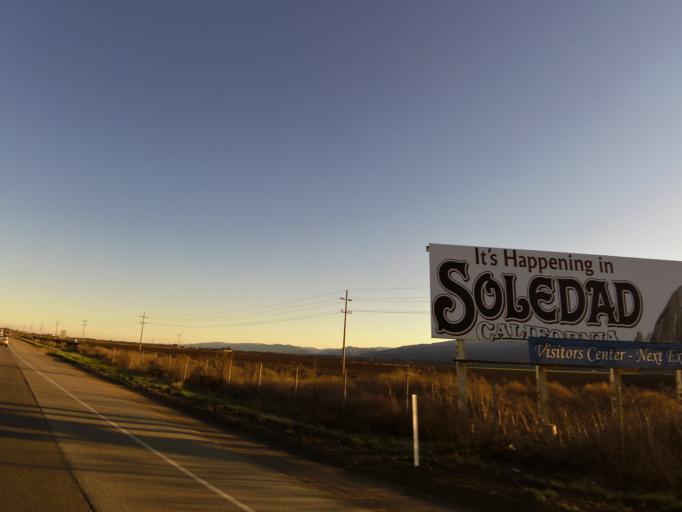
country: US
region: California
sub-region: Monterey County
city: Soledad
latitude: 36.4459
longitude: -121.3594
